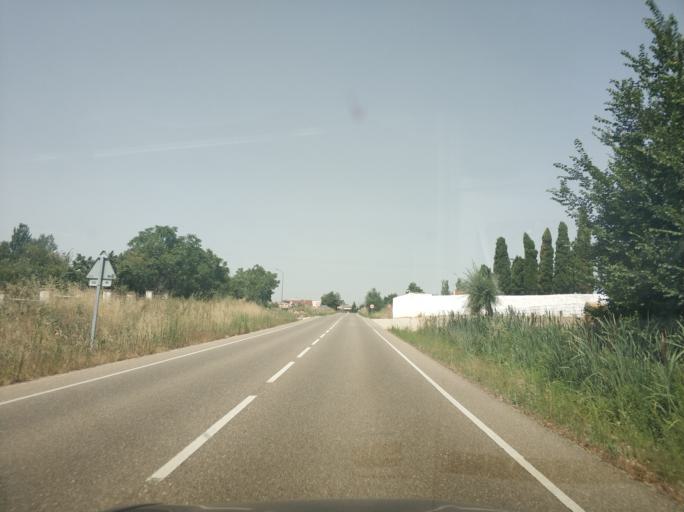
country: ES
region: Castille and Leon
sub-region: Provincia de Salamanca
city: Valverdon
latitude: 41.0452
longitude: -5.7642
